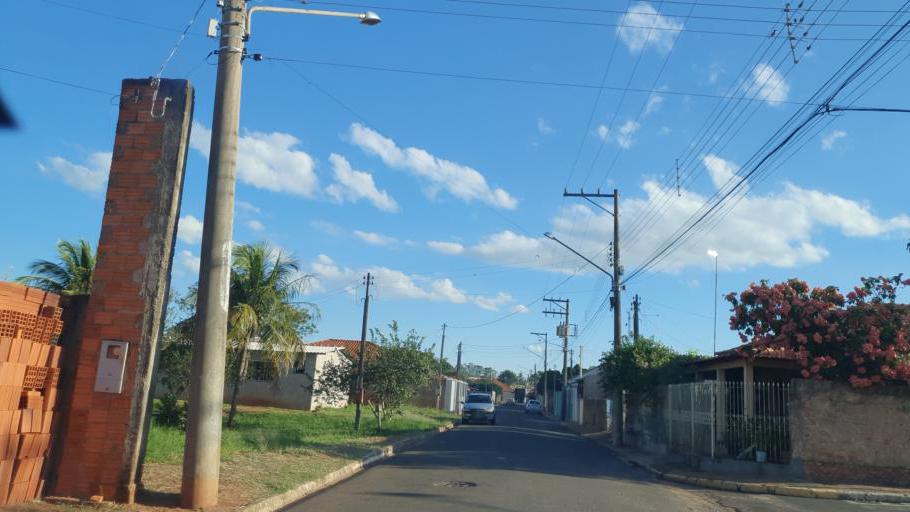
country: BR
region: Sao Paulo
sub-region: Quata
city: Quata
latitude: -22.2520
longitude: -50.7656
